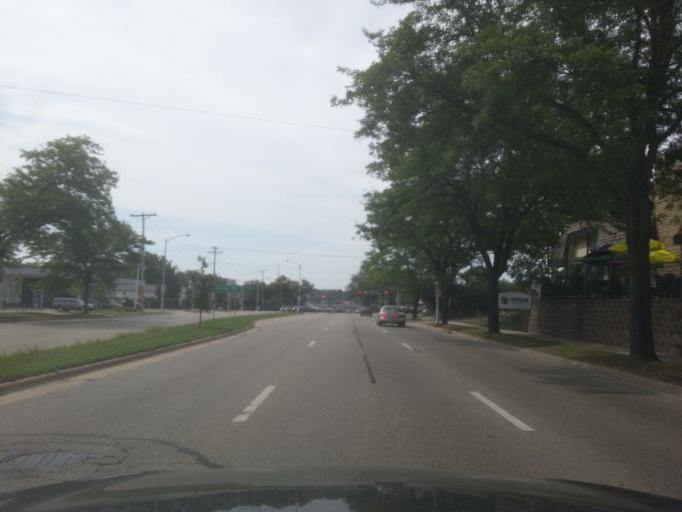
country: US
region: Wisconsin
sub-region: Dane County
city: Shorewood Hills
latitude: 43.0513
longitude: -89.4736
